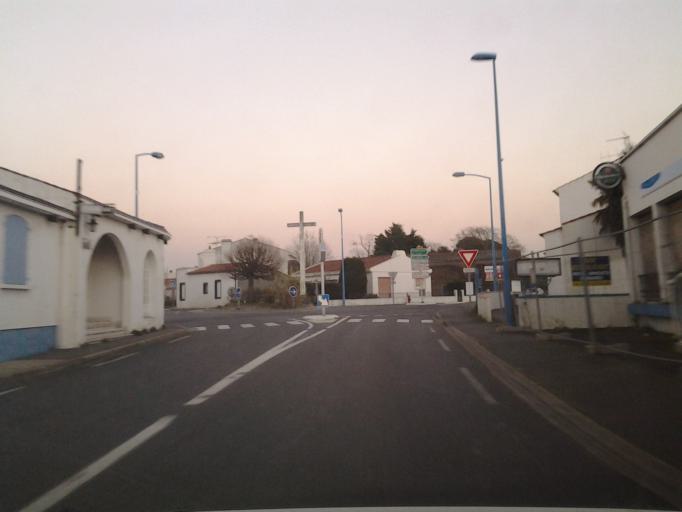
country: FR
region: Pays de la Loire
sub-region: Departement de la Vendee
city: Beauvoir-sur-Mer
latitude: 46.9156
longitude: -2.0470
